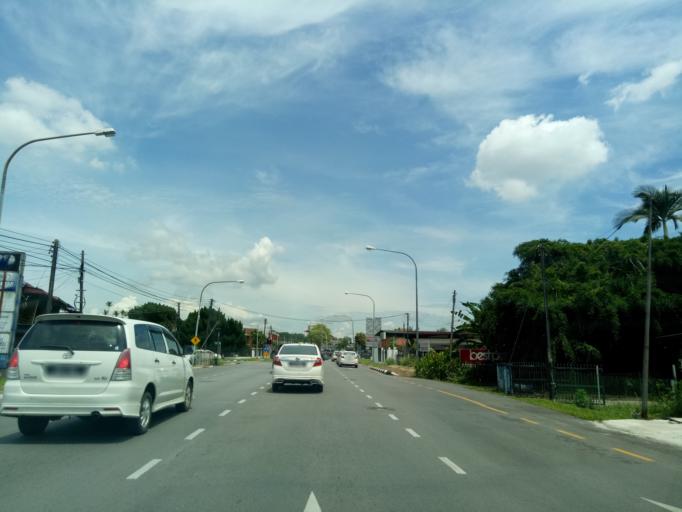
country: MY
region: Sarawak
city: Kuching
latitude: 1.5506
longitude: 110.3555
